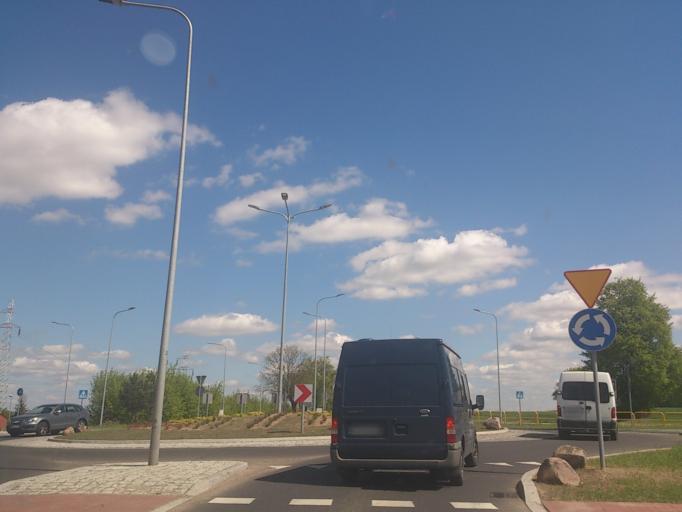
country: PL
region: Podlasie
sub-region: Lomza
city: Lomza
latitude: 53.1730
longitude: 22.0236
